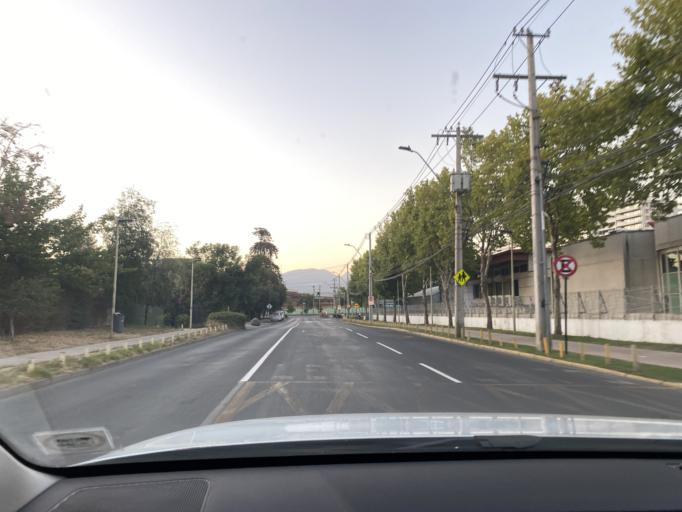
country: CL
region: Santiago Metropolitan
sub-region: Provincia de Santiago
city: Villa Presidente Frei, Nunoa, Santiago, Chile
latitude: -33.3715
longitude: -70.5072
